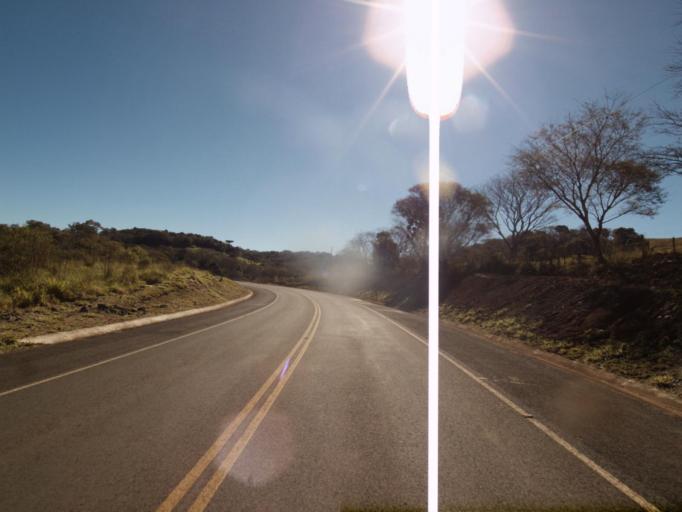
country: AR
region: Misiones
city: Bernardo de Irigoyen
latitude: -26.6186
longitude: -53.6547
